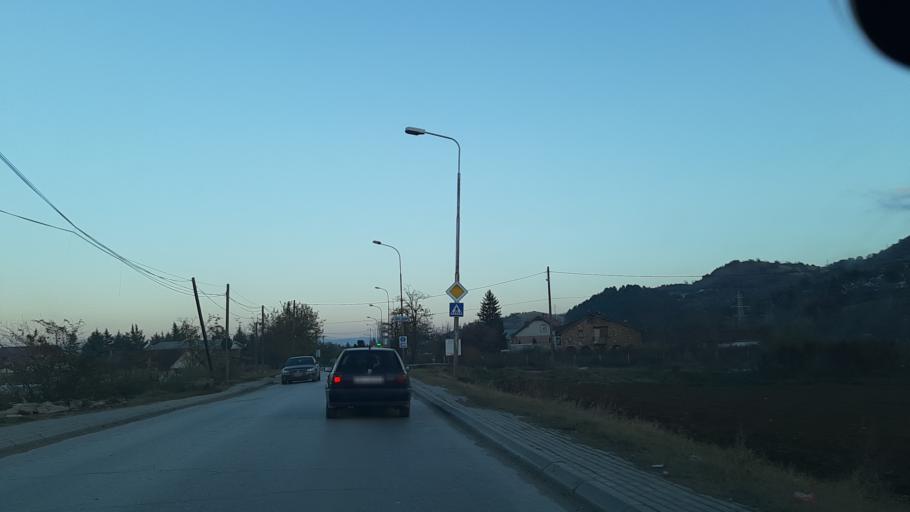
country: MK
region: Kisela Voda
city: Kisela Voda
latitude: 41.9396
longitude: 21.5049
